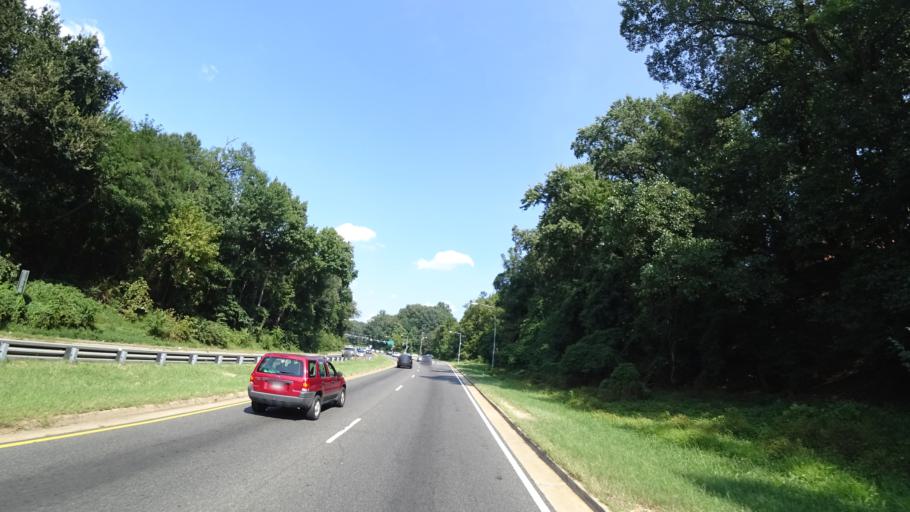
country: US
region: Maryland
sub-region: Prince George's County
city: Hillcrest Heights
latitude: 38.8527
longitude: -76.9855
